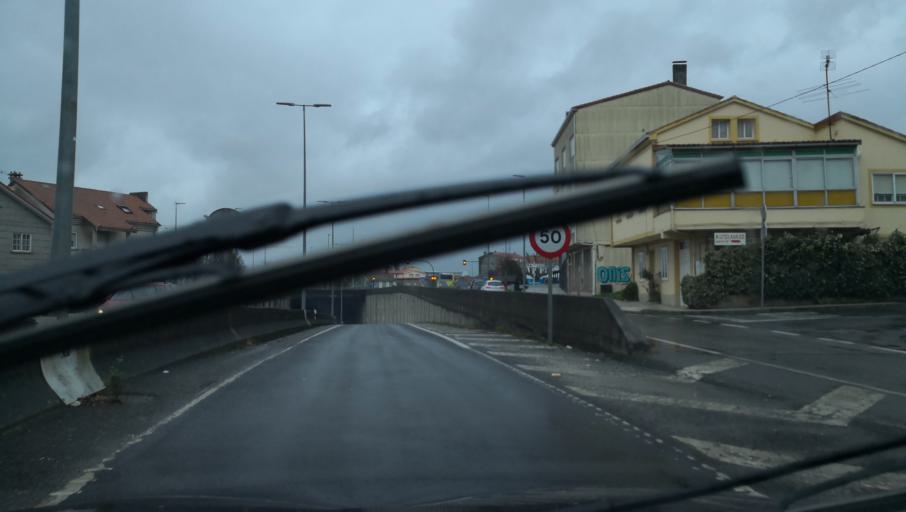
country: ES
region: Galicia
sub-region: Provincia da Coruna
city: Santiago de Compostela
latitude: 42.8589
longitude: -8.5384
